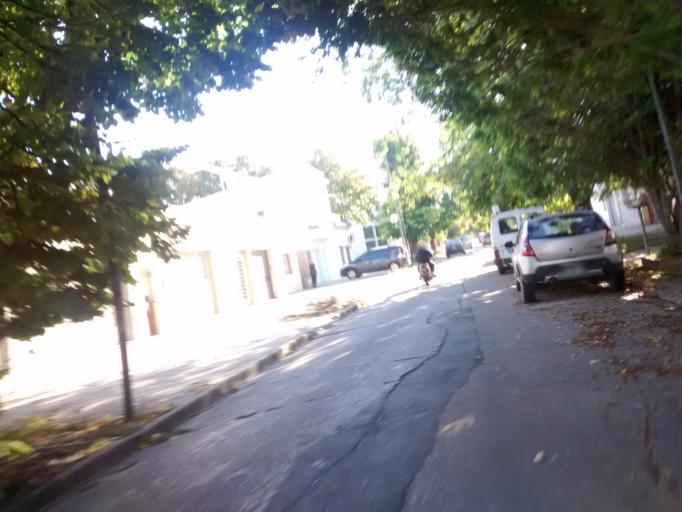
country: AR
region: Buenos Aires
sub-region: Partido de La Plata
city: La Plata
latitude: -34.9360
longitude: -57.9521
